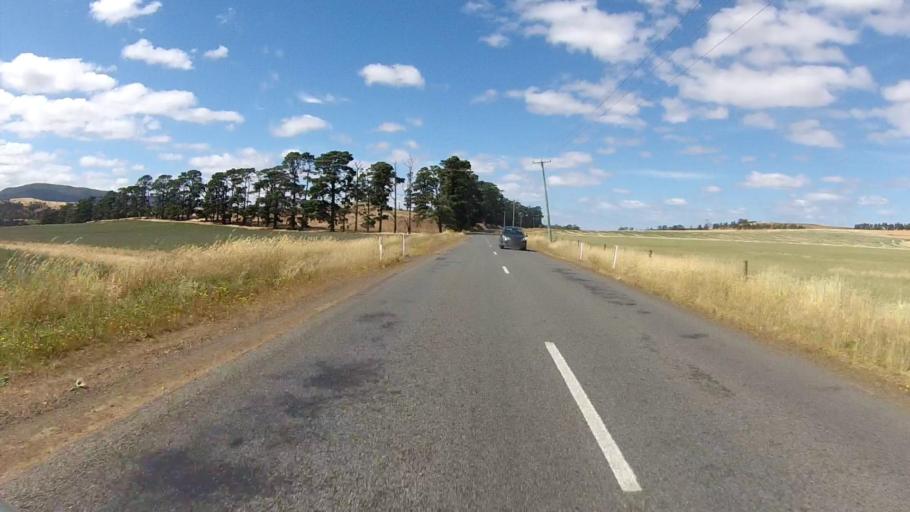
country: AU
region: Tasmania
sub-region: Sorell
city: Sorell
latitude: -42.6358
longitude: 147.4313
